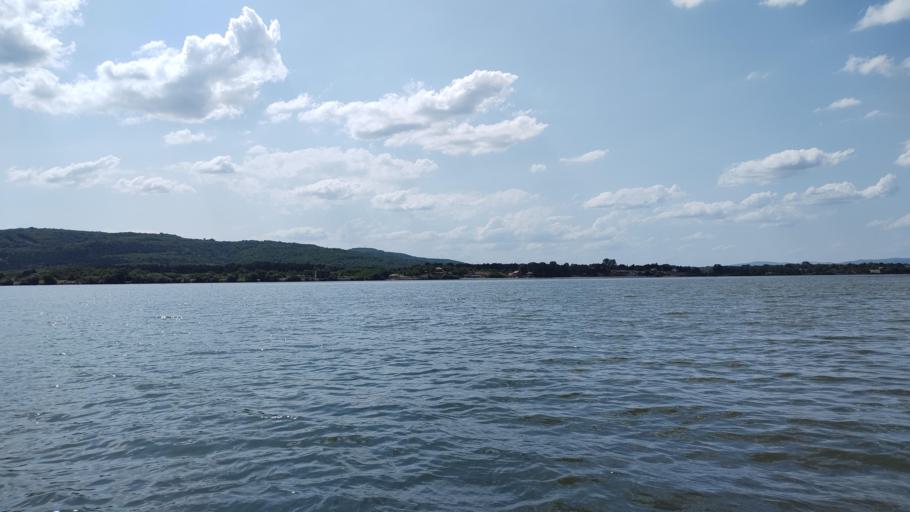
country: RS
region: Central Serbia
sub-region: Branicevski Okrug
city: Golubac
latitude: 44.6745
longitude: 21.6181
